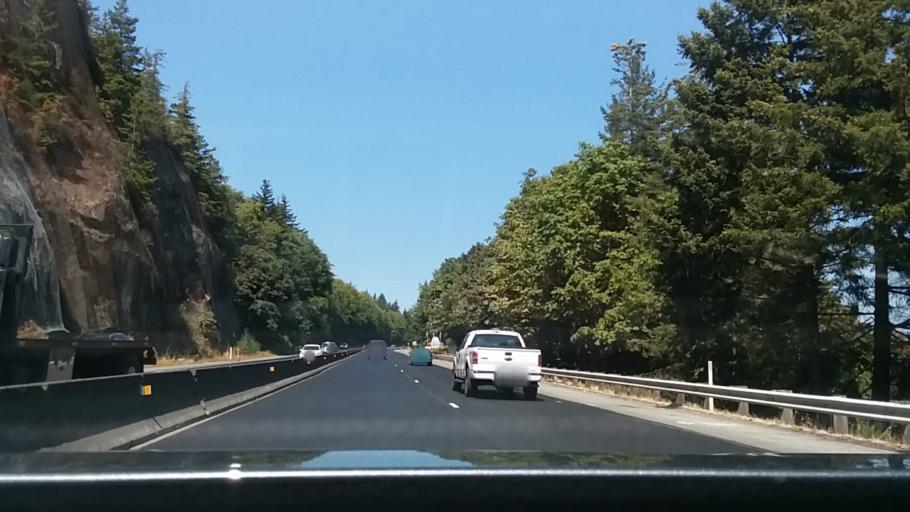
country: US
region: Washington
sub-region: Skagit County
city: Anacortes
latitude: 48.4821
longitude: -122.5946
